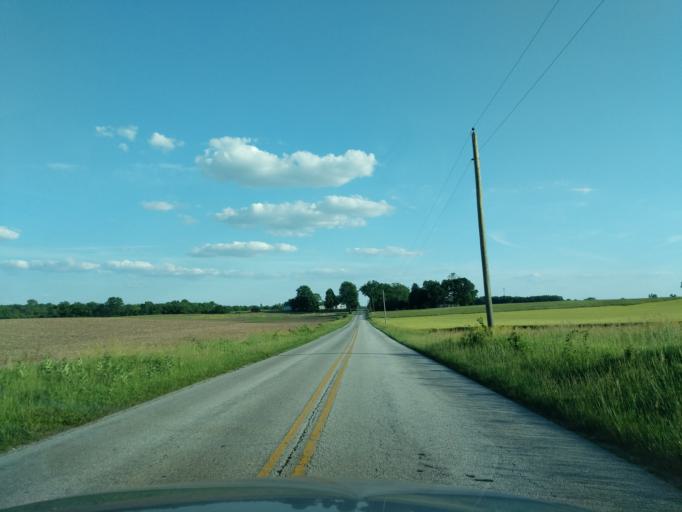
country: US
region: Indiana
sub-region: Huntington County
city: Huntington
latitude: 40.9131
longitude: -85.4714
